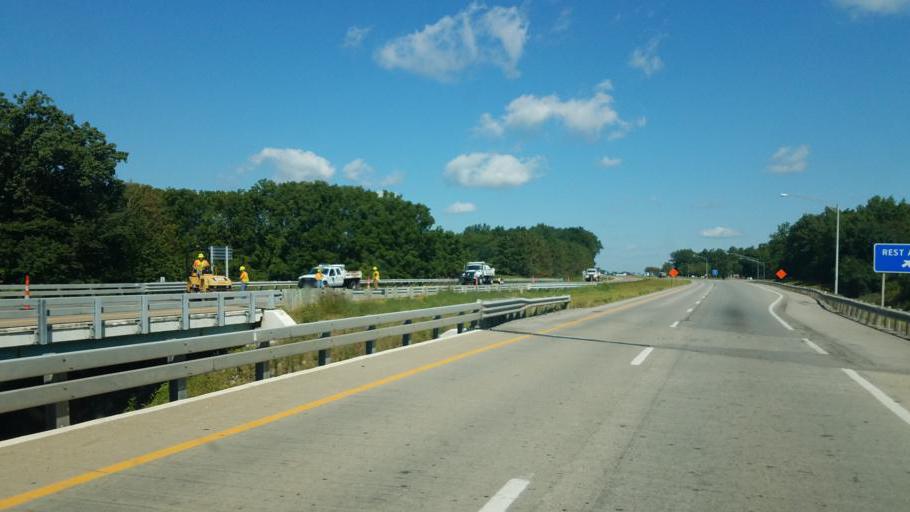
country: US
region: Ohio
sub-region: Wyandot County
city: Carey
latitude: 40.9173
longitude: -83.3543
